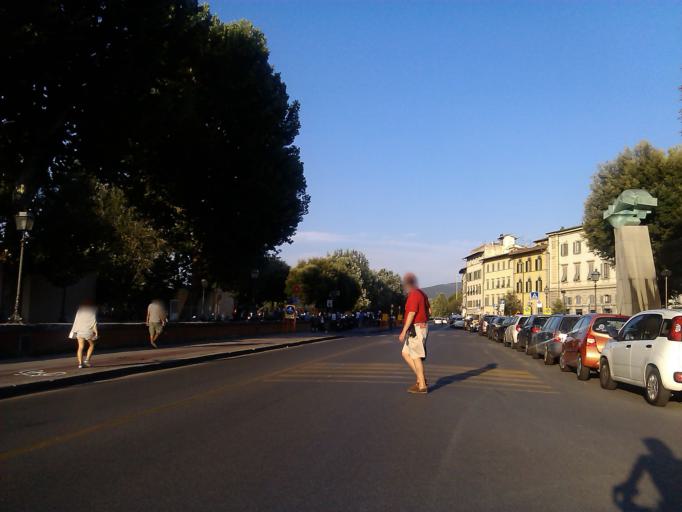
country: IT
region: Tuscany
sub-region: Province of Florence
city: Florence
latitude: 43.7649
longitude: 11.2644
